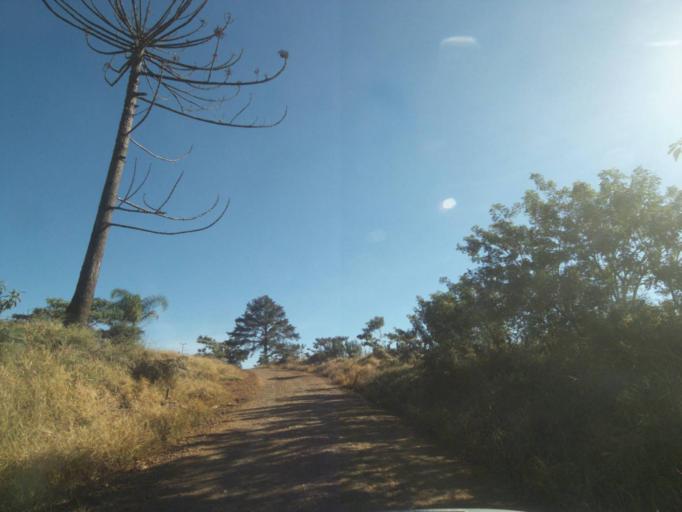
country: BR
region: Parana
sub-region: Tibagi
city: Tibagi
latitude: -24.5421
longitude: -50.5060
